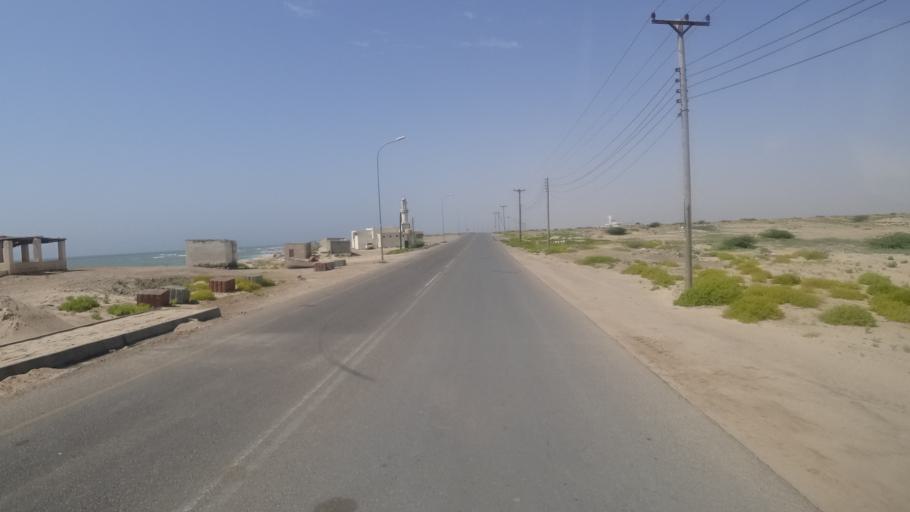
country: OM
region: Ash Sharqiyah
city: Sur
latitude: 22.1124
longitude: 59.7110
